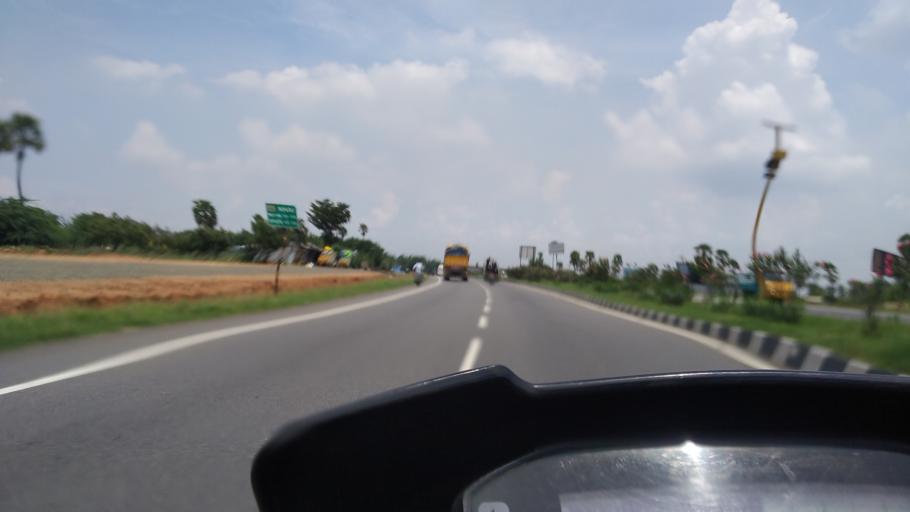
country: IN
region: Tamil Nadu
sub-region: Erode
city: Vijayapuri
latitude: 11.2272
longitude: 77.4673
